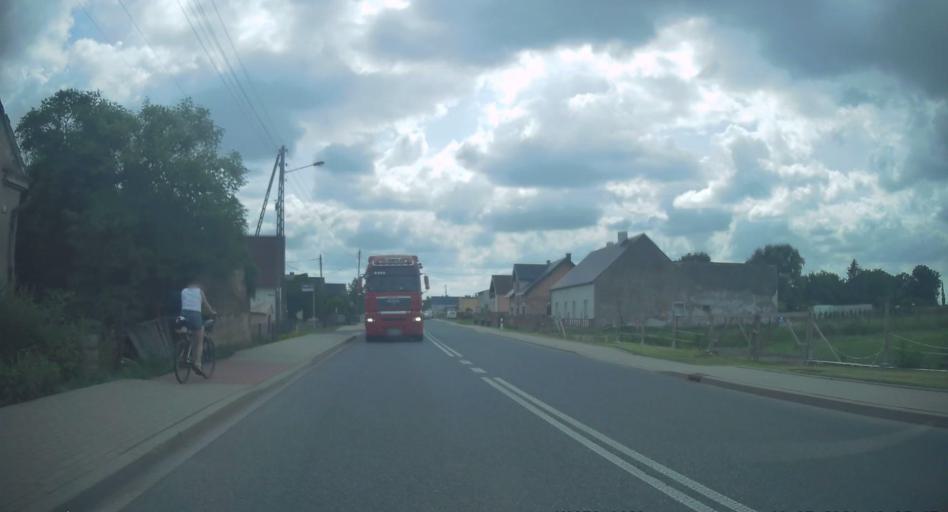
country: PL
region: Opole Voivodeship
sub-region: Powiat prudnicki
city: Glogowek
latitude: 50.3441
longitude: 17.9007
